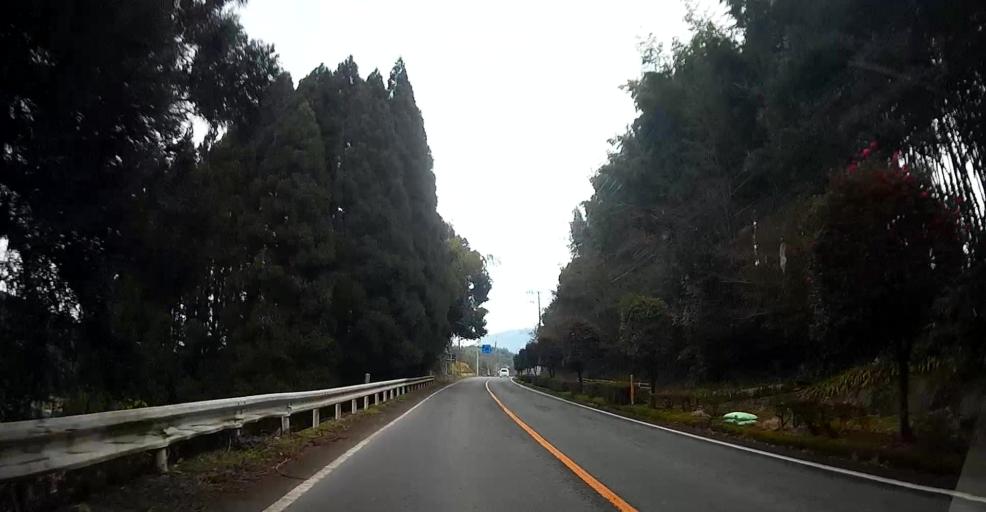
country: JP
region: Kumamoto
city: Matsubase
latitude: 32.6210
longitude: 130.8329
